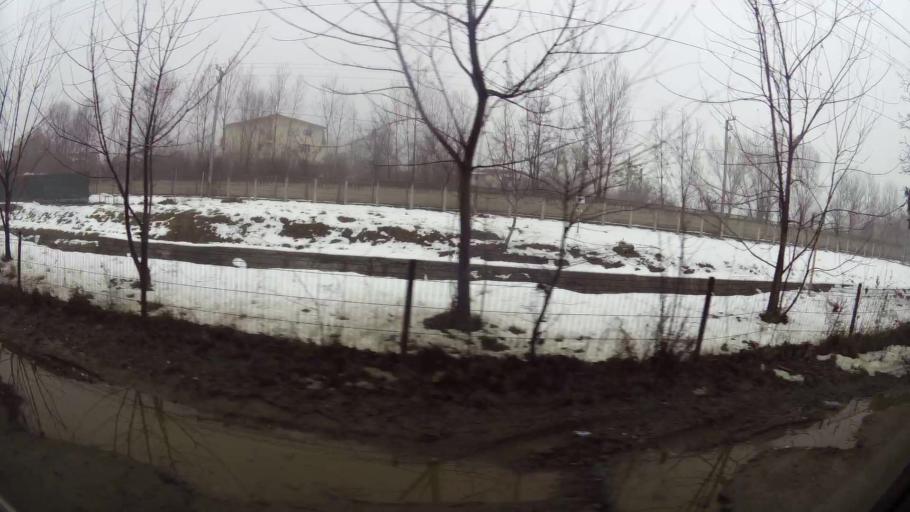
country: RO
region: Ilfov
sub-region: Comuna Chiajna
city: Rosu
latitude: 44.4456
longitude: 26.0186
